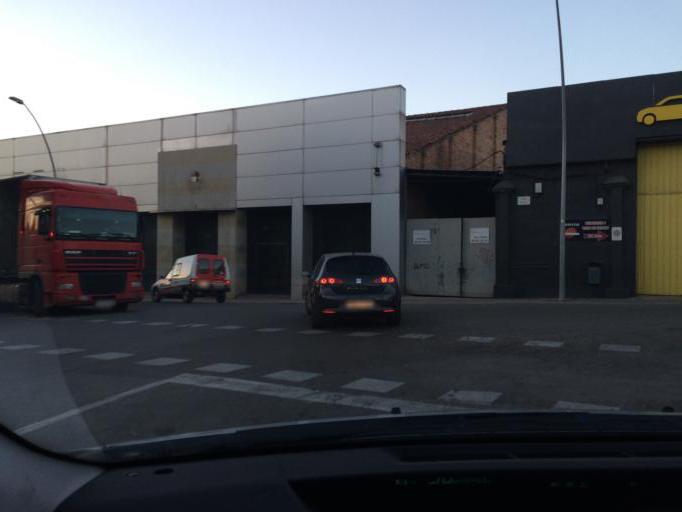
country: ES
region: Catalonia
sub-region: Provincia de Barcelona
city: Manresa
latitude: 41.7212
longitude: 1.8197
